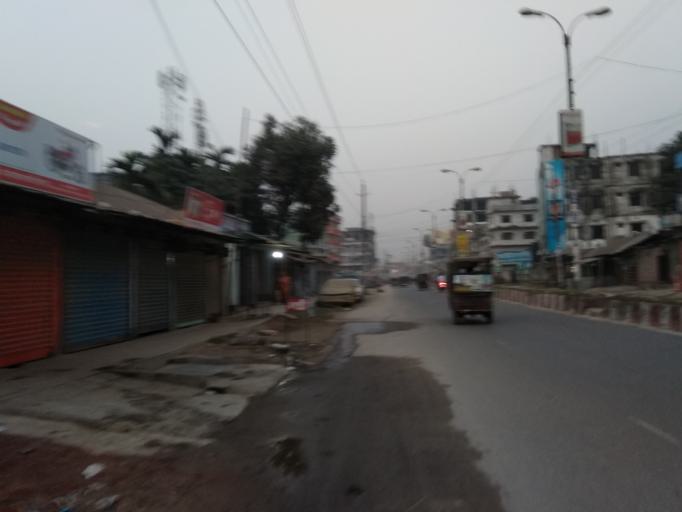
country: BD
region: Rangpur Division
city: Rangpur
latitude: 25.7314
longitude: 89.2547
